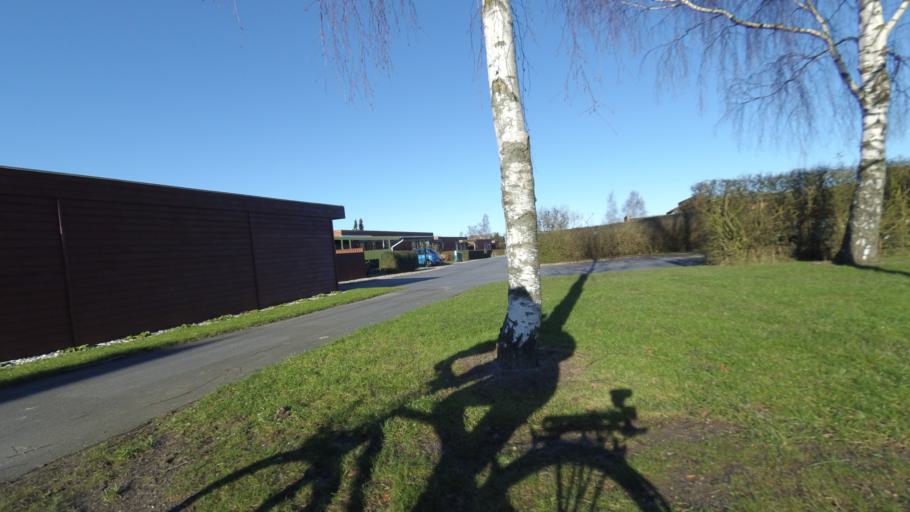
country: DK
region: Central Jutland
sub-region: Arhus Kommune
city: Tranbjerg
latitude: 56.1086
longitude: 10.0992
